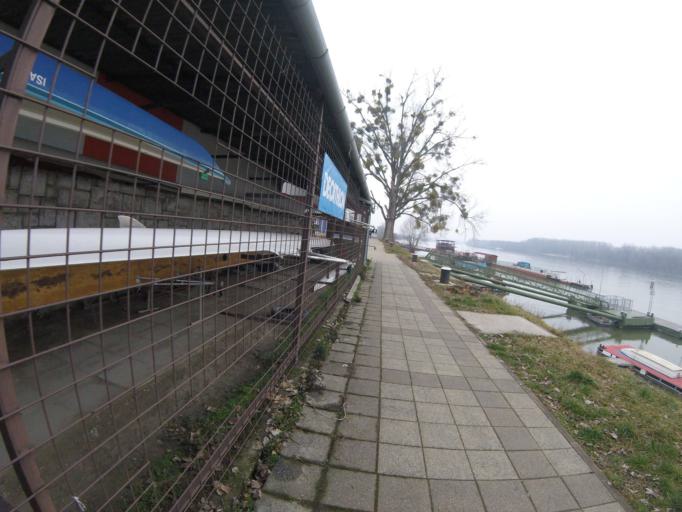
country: HU
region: Baranya
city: Mohacs
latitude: 45.9980
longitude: 18.6894
